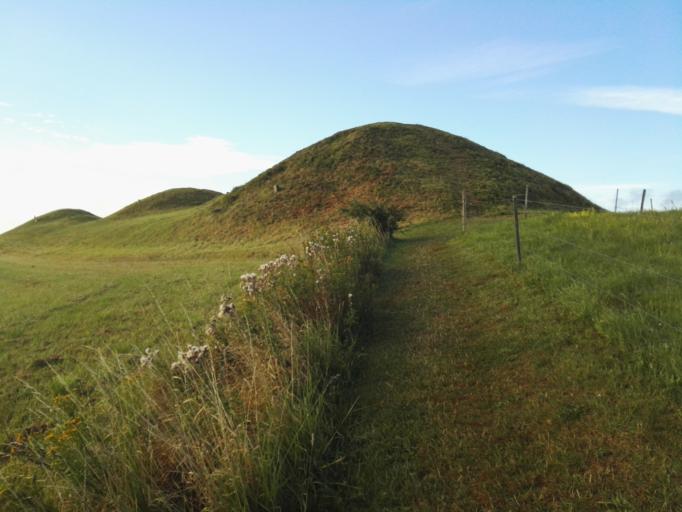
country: DK
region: Zealand
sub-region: Odsherred Kommune
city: Asnaes
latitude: 55.8226
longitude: 11.5370
